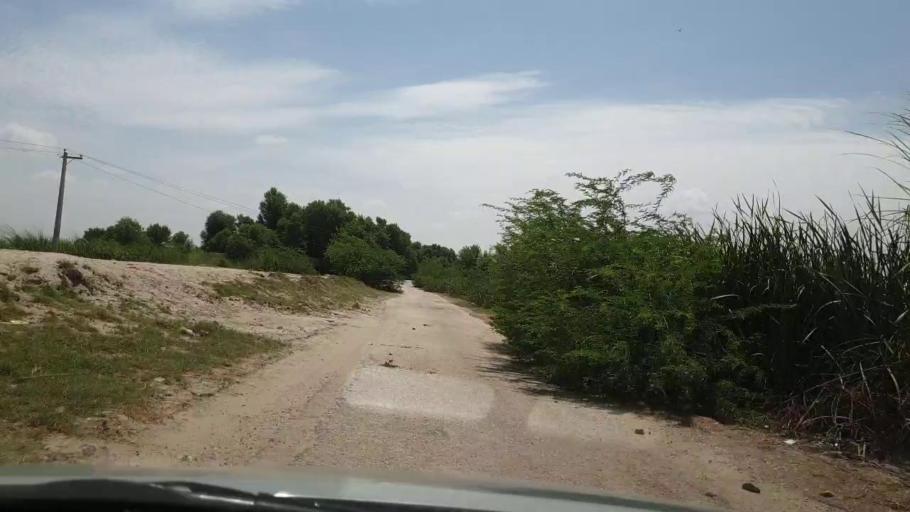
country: PK
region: Sindh
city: Bozdar
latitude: 27.0767
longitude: 68.9692
